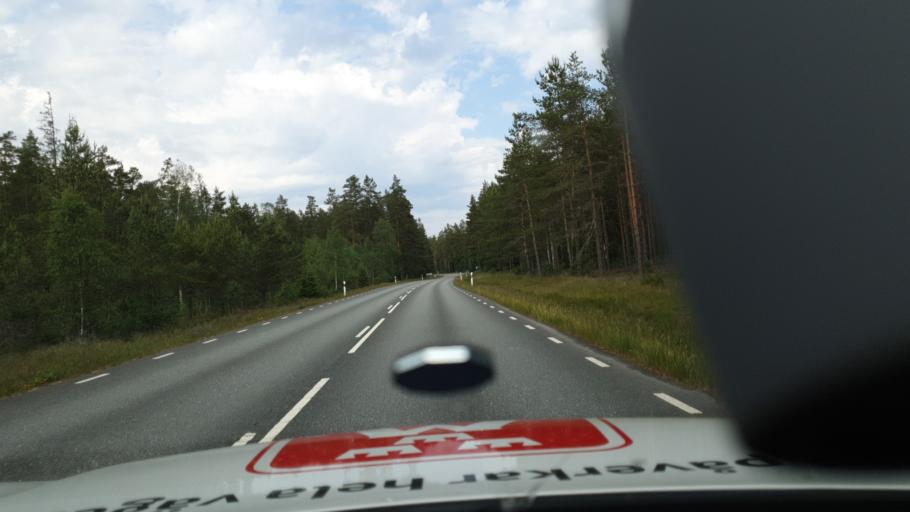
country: SE
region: Joenkoeping
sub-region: Vaggeryds Kommun
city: Skillingaryd
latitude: 57.3199
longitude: 14.0944
